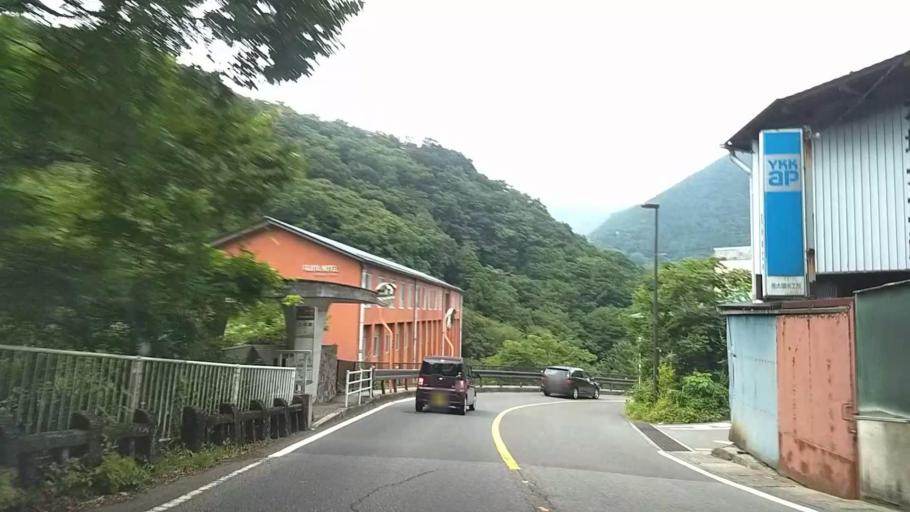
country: JP
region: Kanagawa
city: Hakone
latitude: 35.2421
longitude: 139.0557
